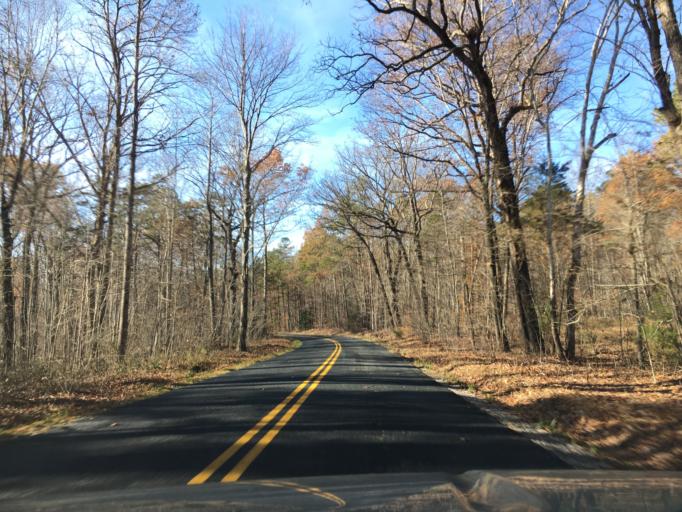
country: US
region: Virginia
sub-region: Buckingham County
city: Buckingham
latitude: 37.4356
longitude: -78.6421
